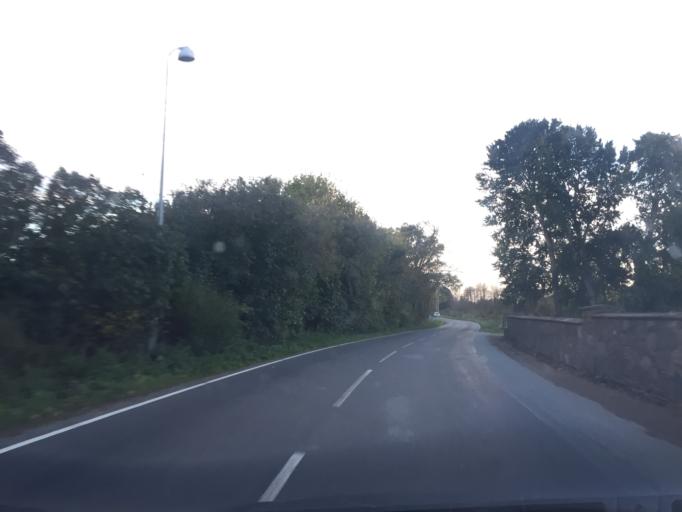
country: DK
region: Capital Region
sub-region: Hoje-Taastrup Kommune
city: Taastrup
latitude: 55.6911
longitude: 12.2457
